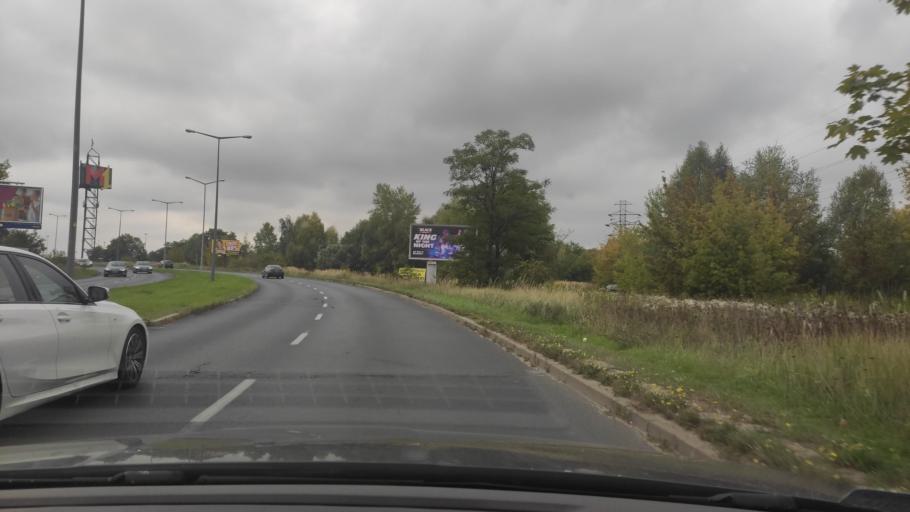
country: PL
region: Greater Poland Voivodeship
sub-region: Poznan
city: Poznan
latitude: 52.3880
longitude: 16.9923
